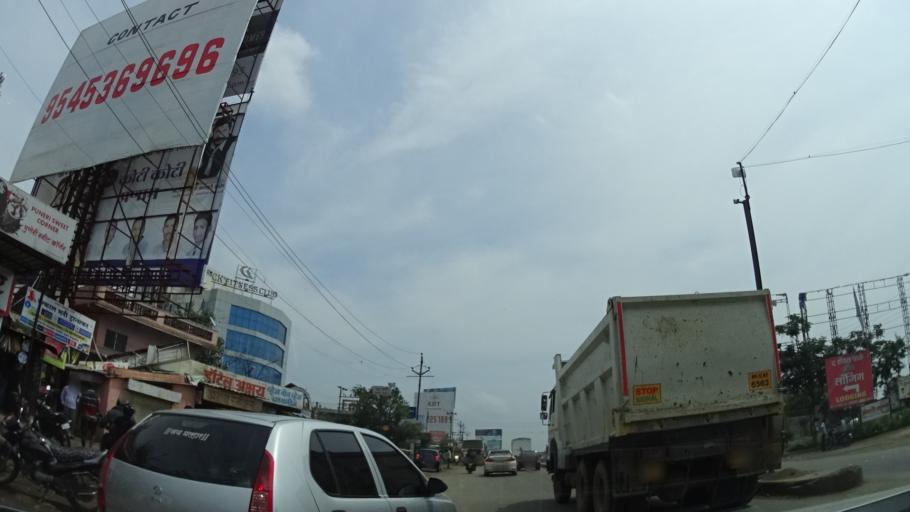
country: IN
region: Maharashtra
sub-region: Pune Division
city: Lohogaon
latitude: 18.5722
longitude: 73.9551
